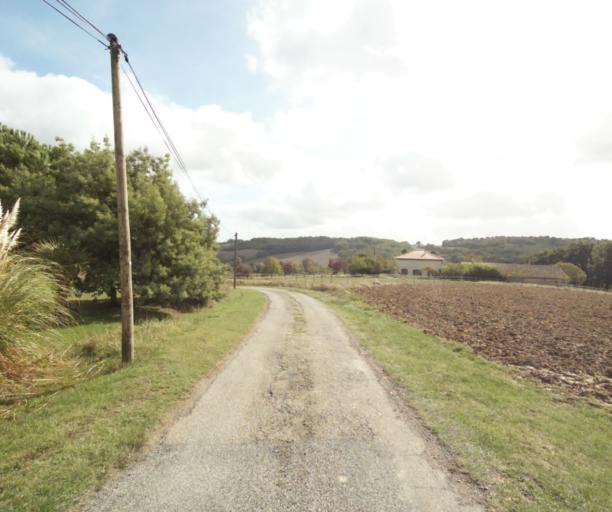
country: FR
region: Midi-Pyrenees
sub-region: Departement du Tarn-et-Garonne
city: Beaumont-de-Lomagne
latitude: 43.8619
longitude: 1.0942
